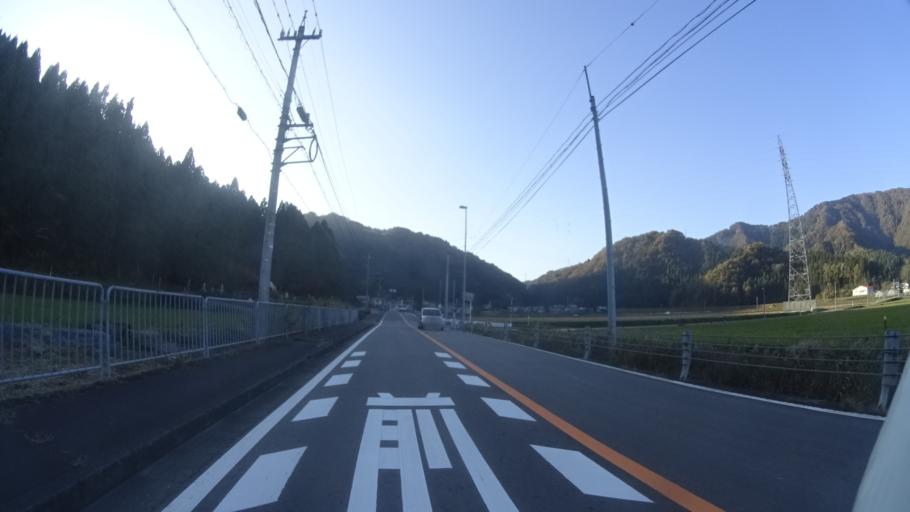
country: JP
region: Fukui
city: Ono
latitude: 35.9947
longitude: 136.4636
